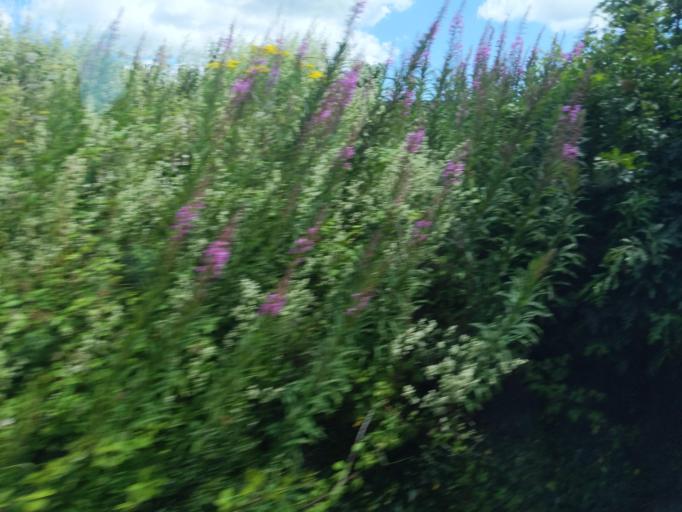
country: GB
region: England
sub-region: Cornwall
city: Lostwithiel
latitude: 50.3752
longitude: -4.6825
